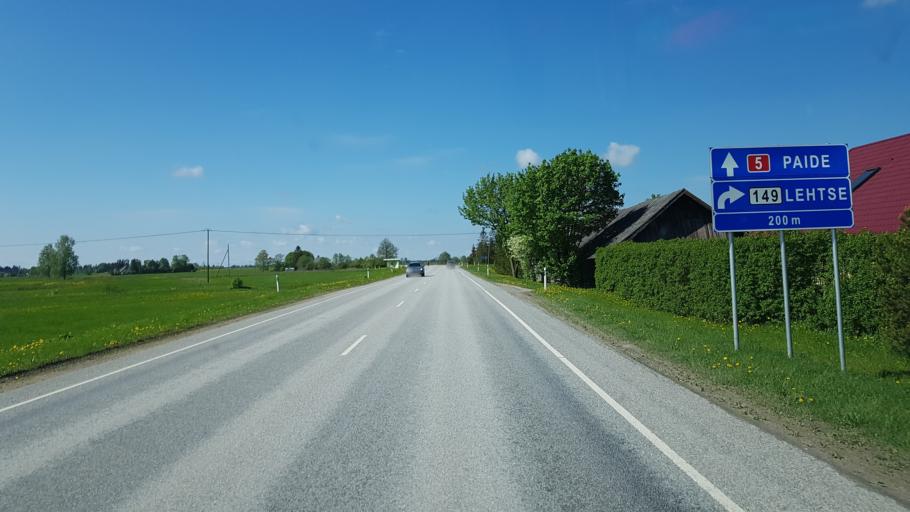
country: EE
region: Laeaene-Virumaa
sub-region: Tapa vald
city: Tapa
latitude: 59.2218
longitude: 25.8943
